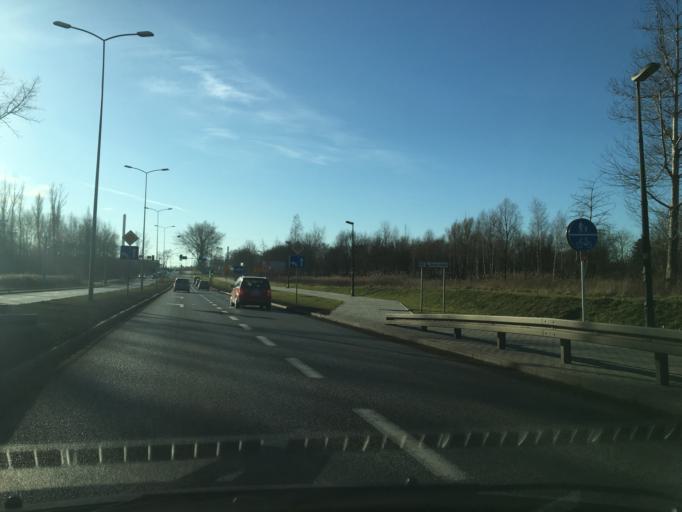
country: PL
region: Silesian Voivodeship
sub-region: Swietochlowice
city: Swietochlowice
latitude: 50.2994
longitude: 18.8799
